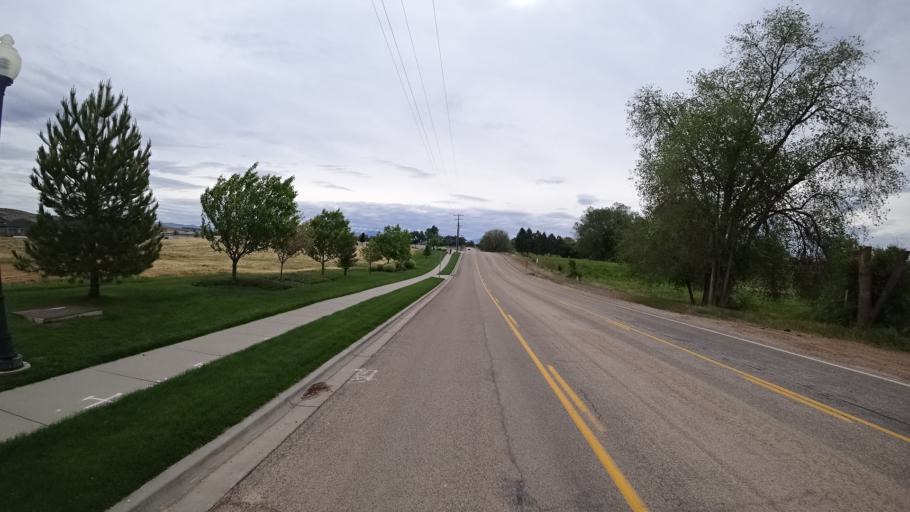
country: US
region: Idaho
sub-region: Ada County
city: Star
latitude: 43.7175
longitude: -116.4950
